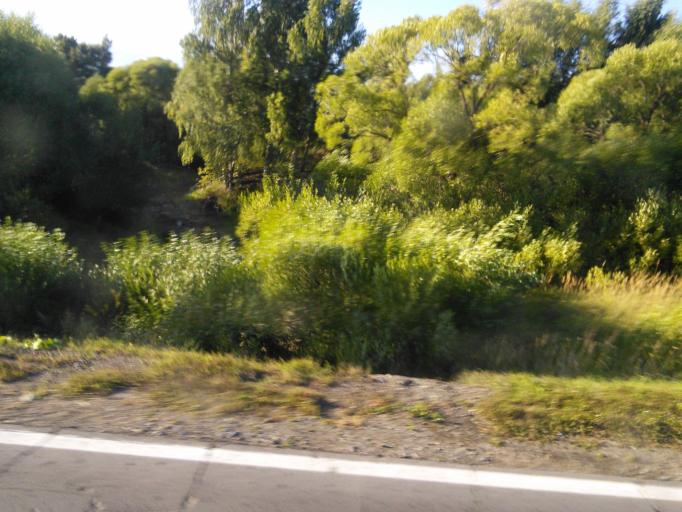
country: RU
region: Jaroslavl
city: Poshekhon'ye
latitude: 58.4817
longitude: 39.0601
